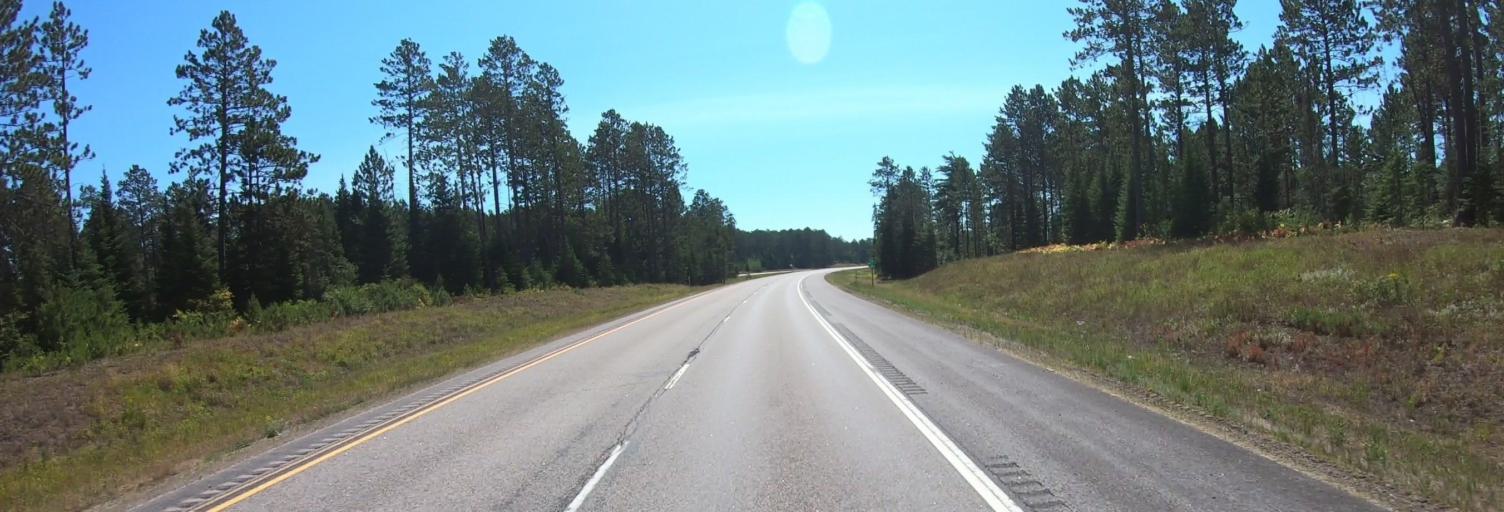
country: US
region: Minnesota
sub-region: Saint Louis County
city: Parkville
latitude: 47.6572
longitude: -92.5754
